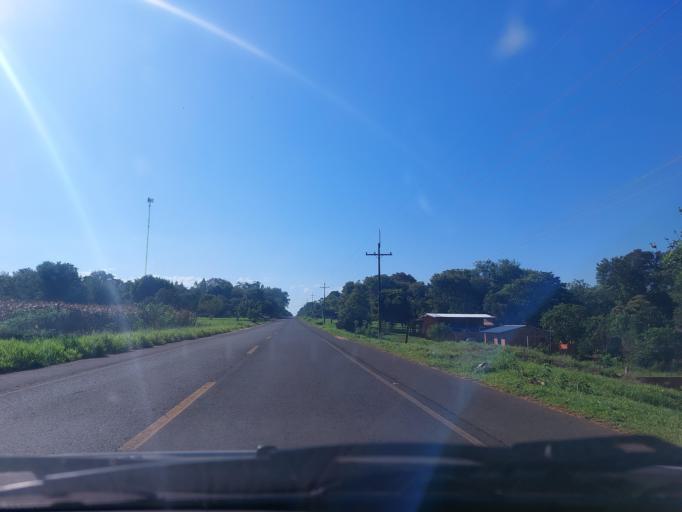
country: PY
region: San Pedro
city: Guayaybi
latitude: -24.5319
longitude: -56.4939
